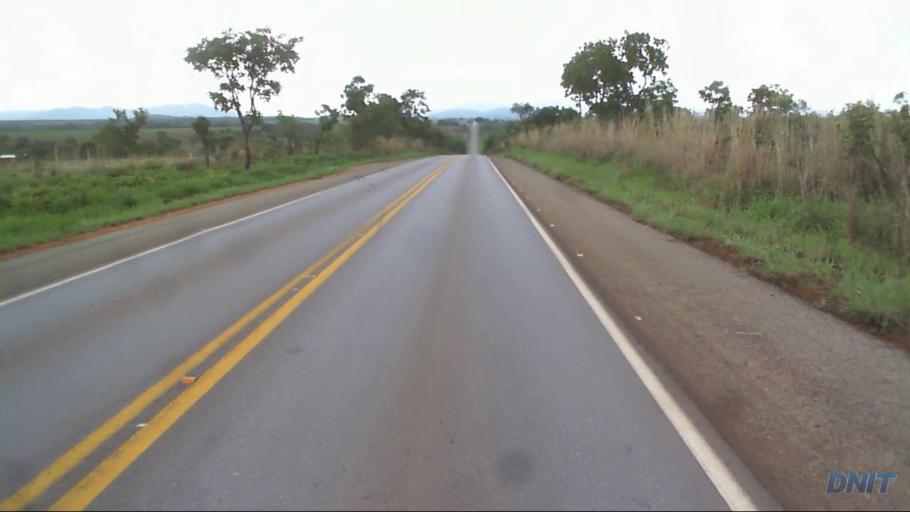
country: BR
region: Goias
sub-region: Barro Alto
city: Barro Alto
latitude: -14.8016
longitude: -49.0482
